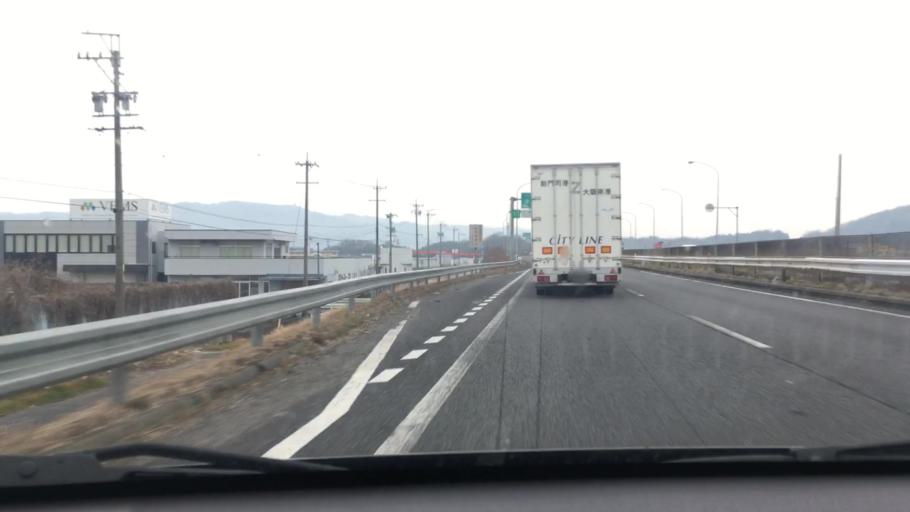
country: JP
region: Mie
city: Ueno-ebisumachi
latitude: 34.7680
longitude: 136.1565
